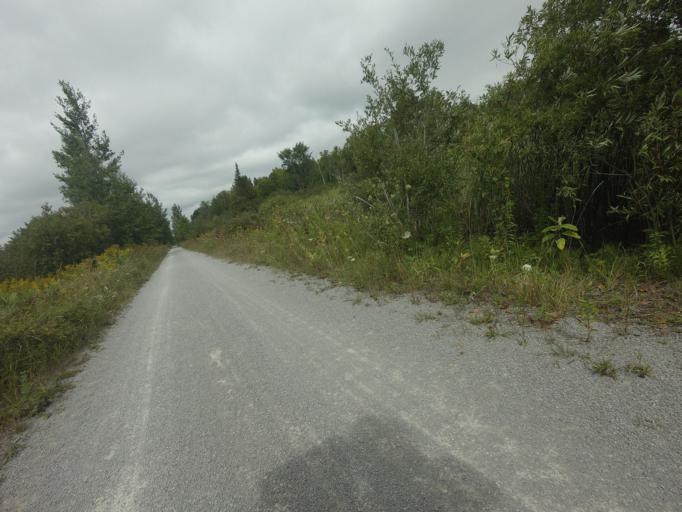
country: CA
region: Ontario
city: Uxbridge
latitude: 44.2066
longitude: -79.0625
